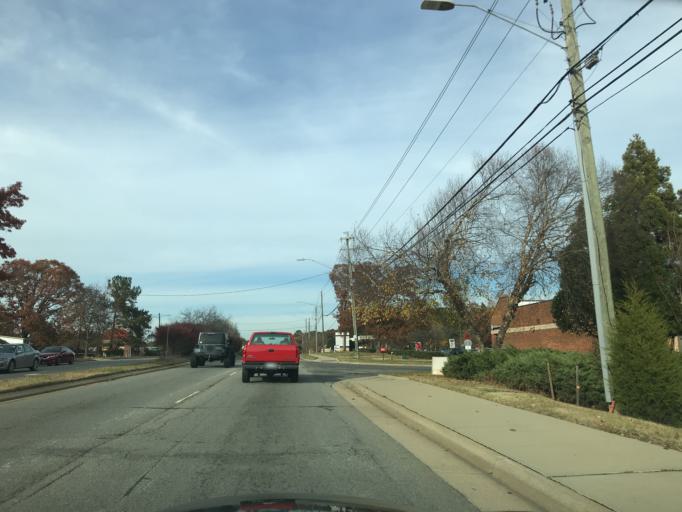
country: US
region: North Carolina
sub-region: Wake County
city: West Raleigh
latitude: 35.8706
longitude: -78.6798
